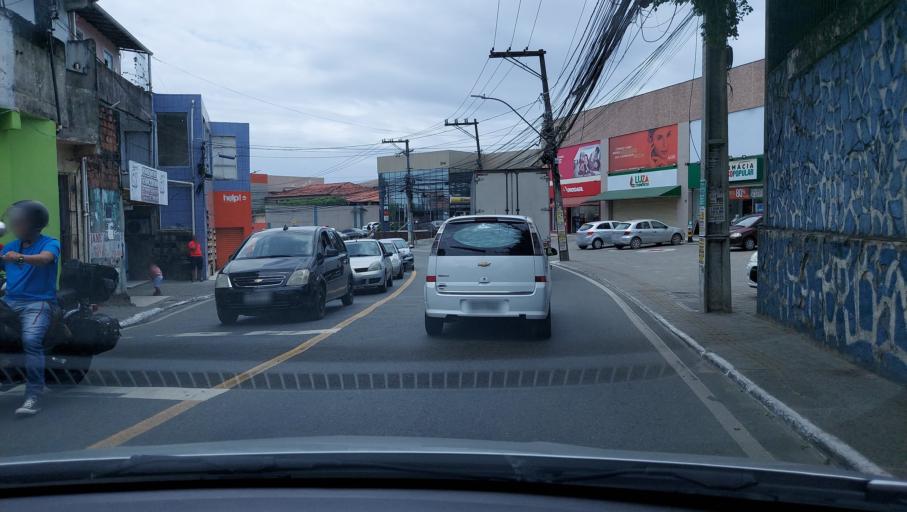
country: BR
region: Bahia
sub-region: Salvador
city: Salvador
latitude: -12.9538
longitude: -38.4613
